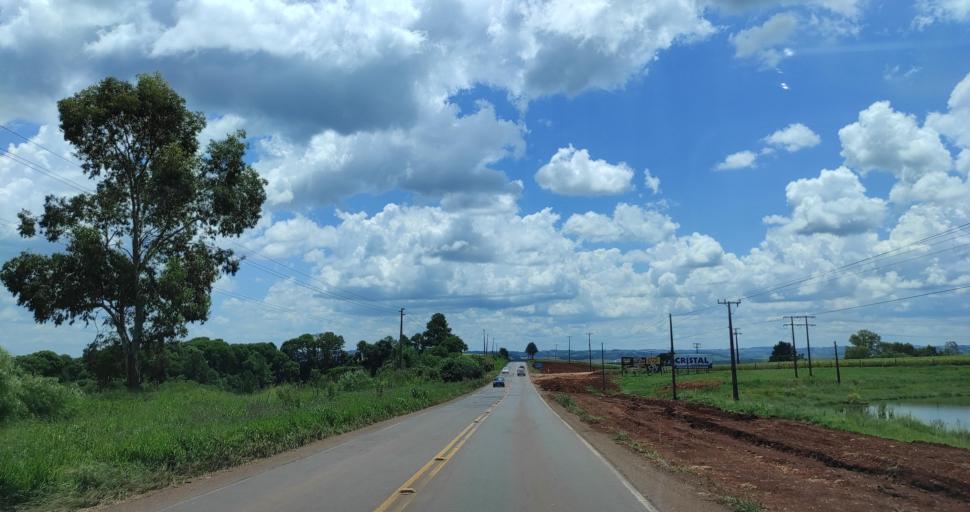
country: BR
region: Santa Catarina
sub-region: Xanxere
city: Xanxere
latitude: -26.7838
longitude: -52.4079
